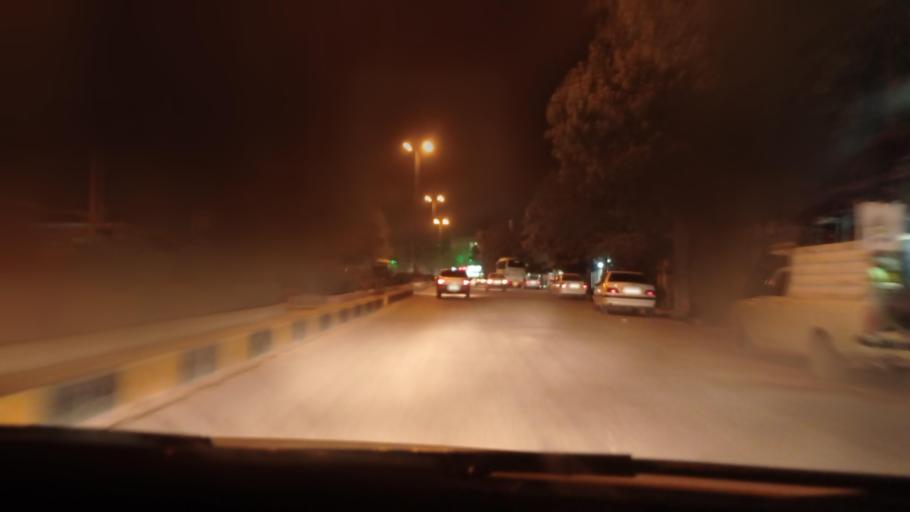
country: IR
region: Lorestan
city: Kuhdasht
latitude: 33.5380
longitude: 47.6114
